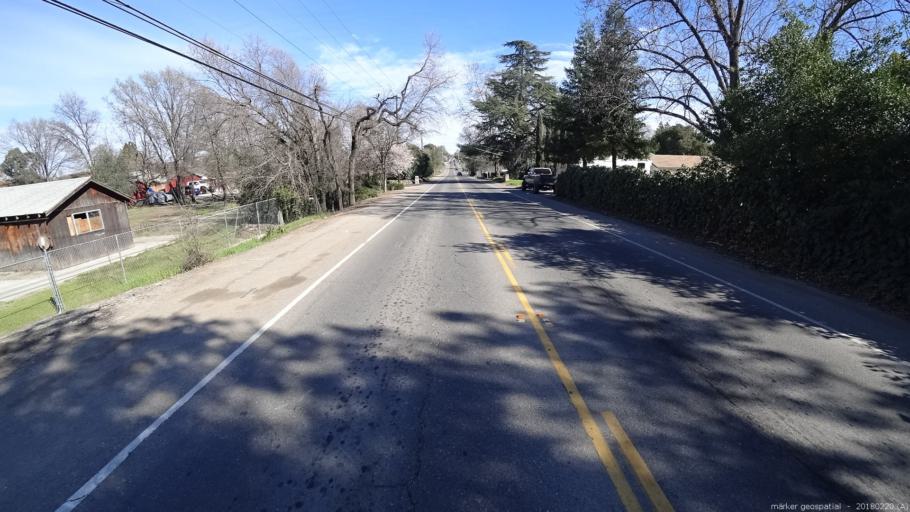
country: US
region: California
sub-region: Sacramento County
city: Orangevale
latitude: 38.6999
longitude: -121.2061
